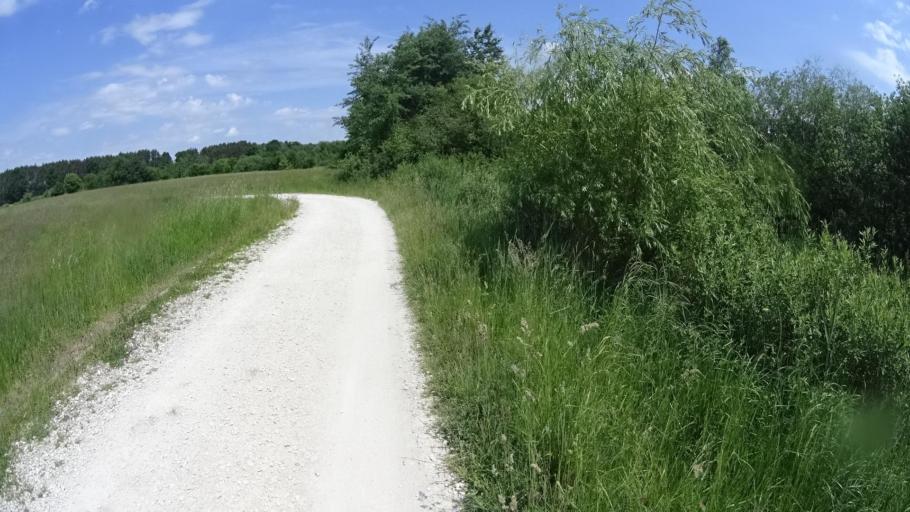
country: PL
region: Masovian Voivodeship
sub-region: Powiat warszawski zachodni
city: Stare Babice
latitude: 52.2683
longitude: 20.8457
